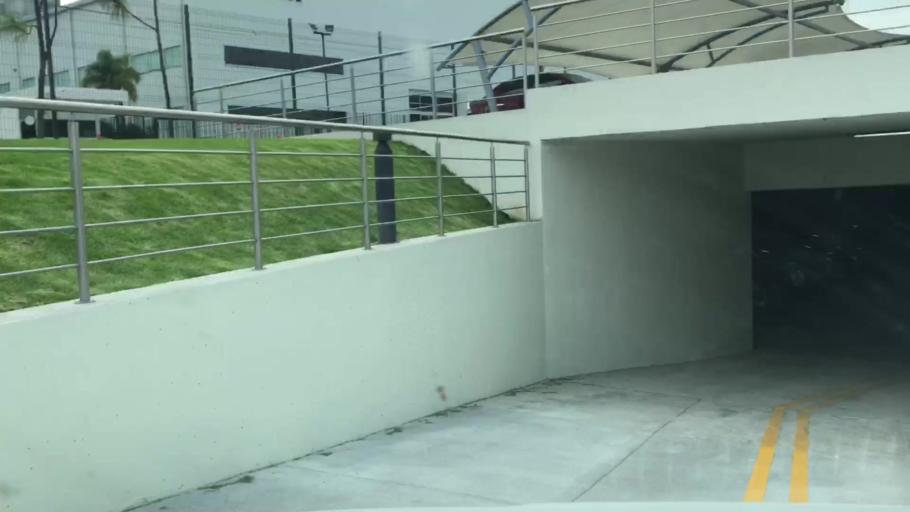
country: MX
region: Jalisco
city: Zapopan2
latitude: 20.6830
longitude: -103.4570
